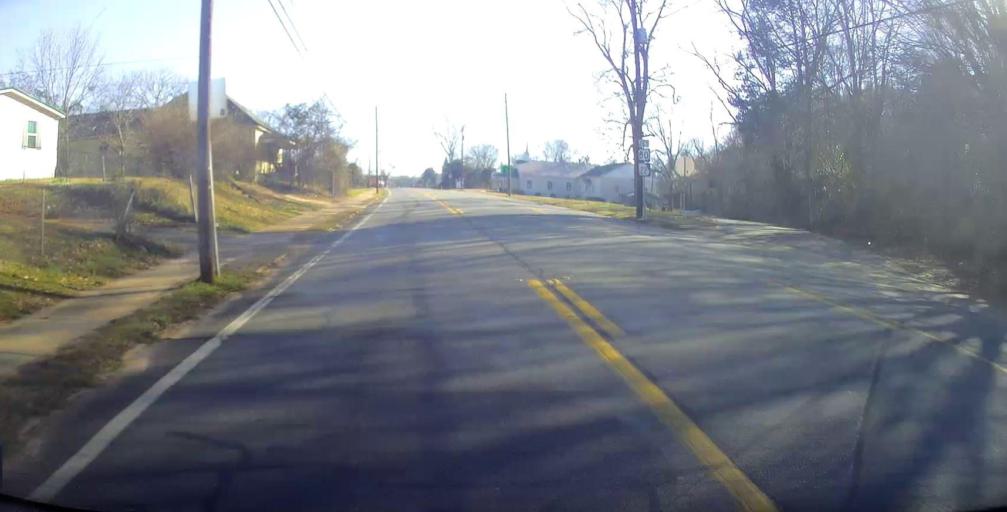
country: US
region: Georgia
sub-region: Talbot County
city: Talbotton
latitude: 32.6824
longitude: -84.5401
